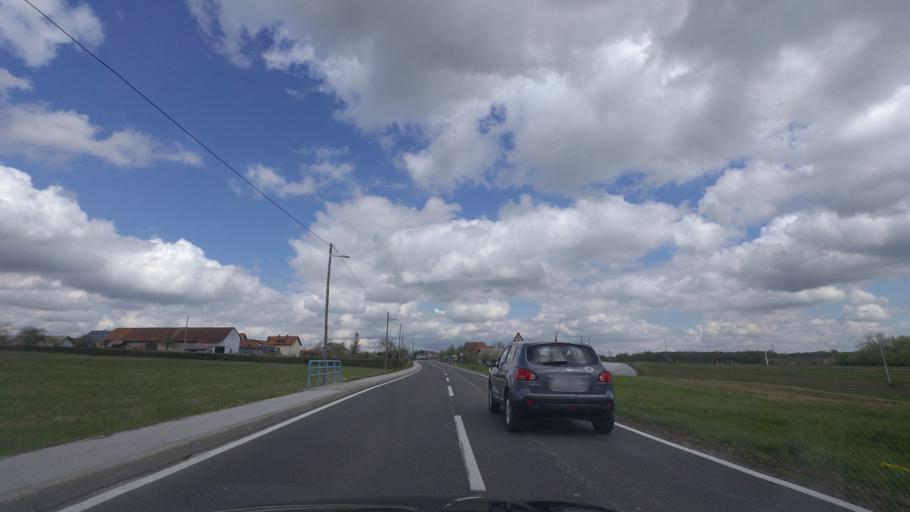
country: HR
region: Grad Zagreb
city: Horvati
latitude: 45.7083
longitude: 15.7734
